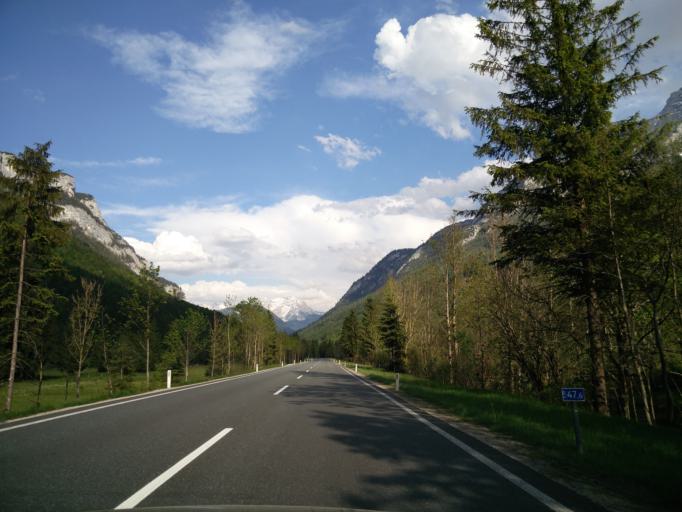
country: AT
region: Tyrol
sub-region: Politischer Bezirk Kitzbuhel
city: Waidring
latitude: 47.5858
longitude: 12.6172
